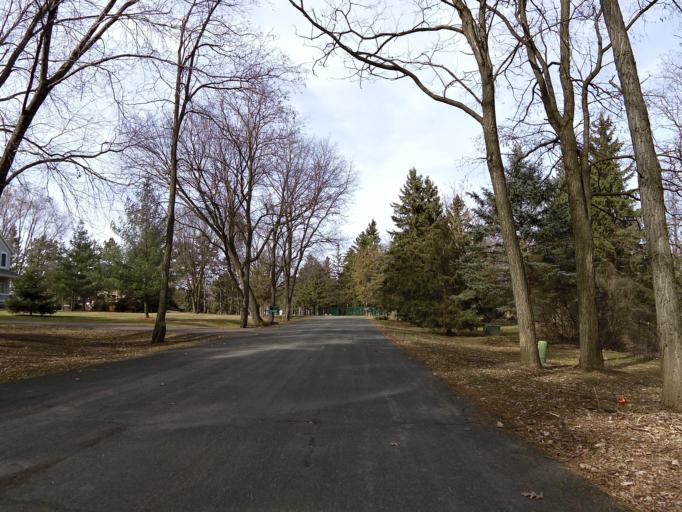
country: US
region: Minnesota
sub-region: Washington County
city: Lakeland
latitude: 44.9432
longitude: -92.7831
